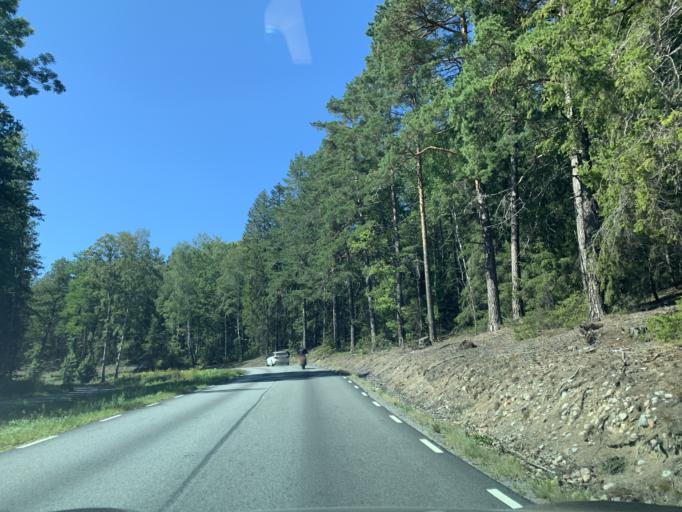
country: SE
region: Stockholm
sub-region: Botkyrka Kommun
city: Fittja
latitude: 59.2735
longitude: 17.8414
